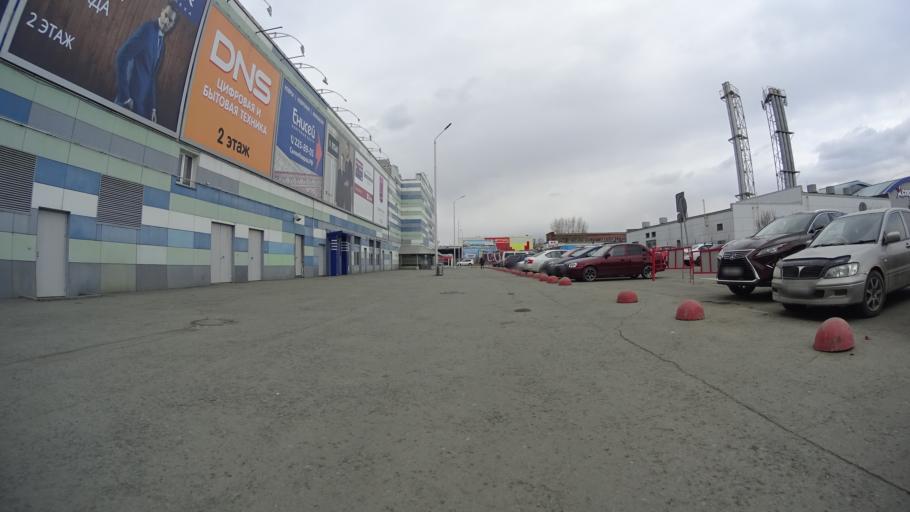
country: RU
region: Chelyabinsk
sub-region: Gorod Chelyabinsk
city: Chelyabinsk
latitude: 55.1644
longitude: 61.4317
